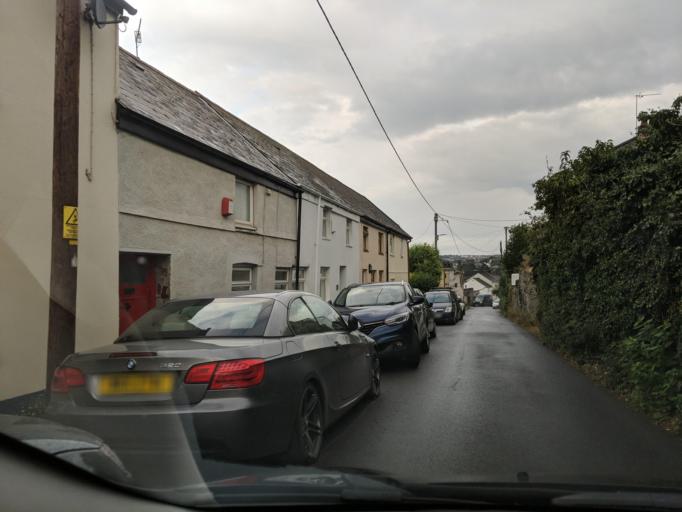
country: GB
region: England
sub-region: Devon
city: Plympton
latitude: 50.3855
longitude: -4.0629
